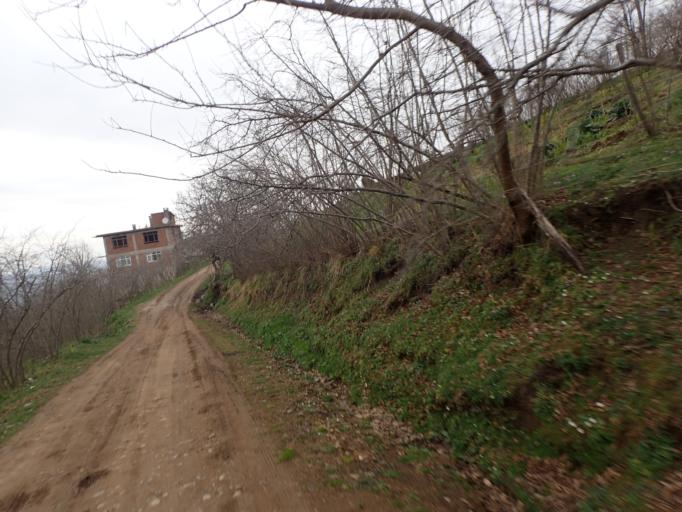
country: TR
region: Ordu
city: Camas
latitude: 40.9152
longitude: 37.5179
